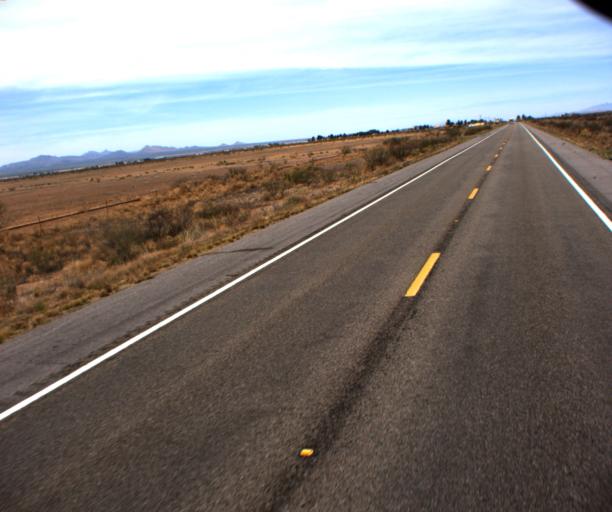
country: US
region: Arizona
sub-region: Cochise County
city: Pirtleville
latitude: 31.5826
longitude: -109.6688
